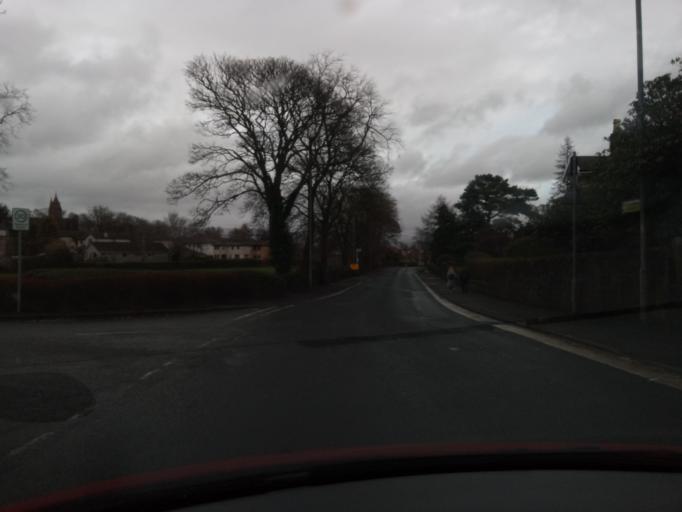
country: GB
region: Scotland
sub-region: East Dunbartonshire
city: Kirkintilloch
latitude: 55.9257
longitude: -4.1567
